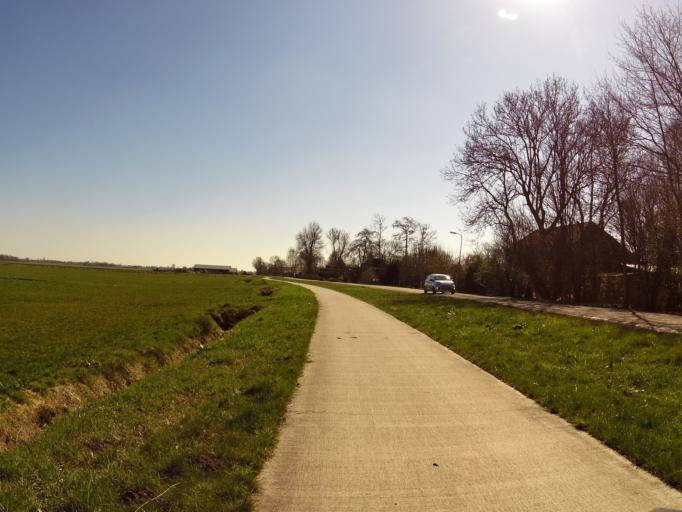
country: NL
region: Overijssel
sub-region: Gemeente Steenwijkerland
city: Blokzijl
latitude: 52.7644
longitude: 5.9925
